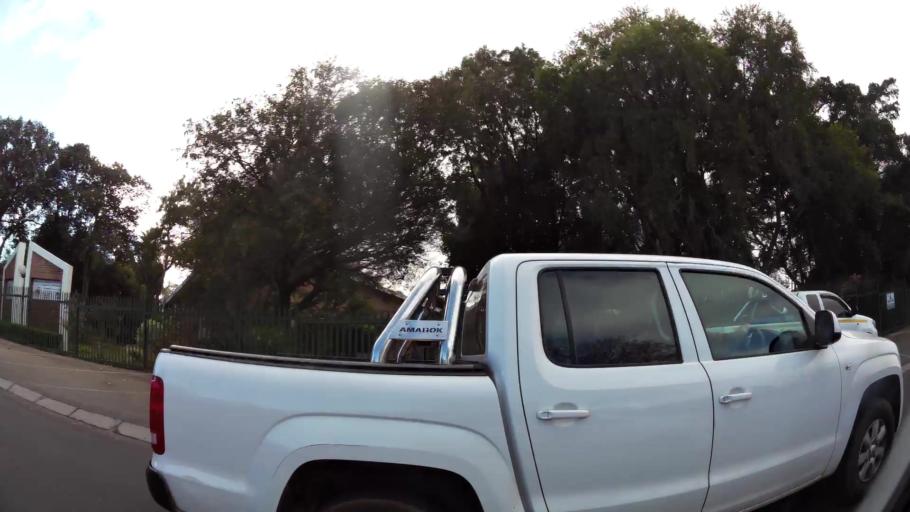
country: ZA
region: Limpopo
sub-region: Capricorn District Municipality
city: Polokwane
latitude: -23.9089
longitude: 29.4742
